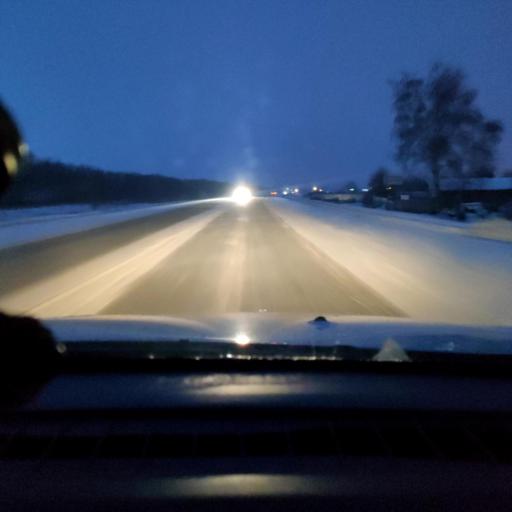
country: RU
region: Samara
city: Kinel'-Cherkassy
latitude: 53.4184
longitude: 51.4688
